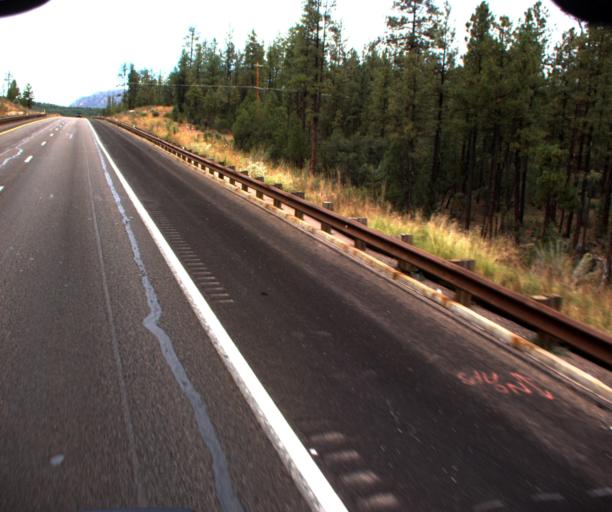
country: US
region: Arizona
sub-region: Gila County
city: Star Valley
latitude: 34.3108
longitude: -111.1103
